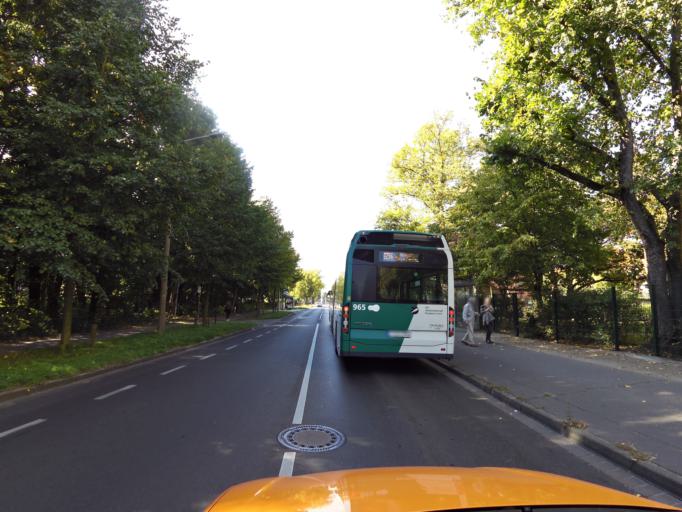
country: DE
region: Berlin
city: Wannsee
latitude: 52.3809
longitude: 13.1356
